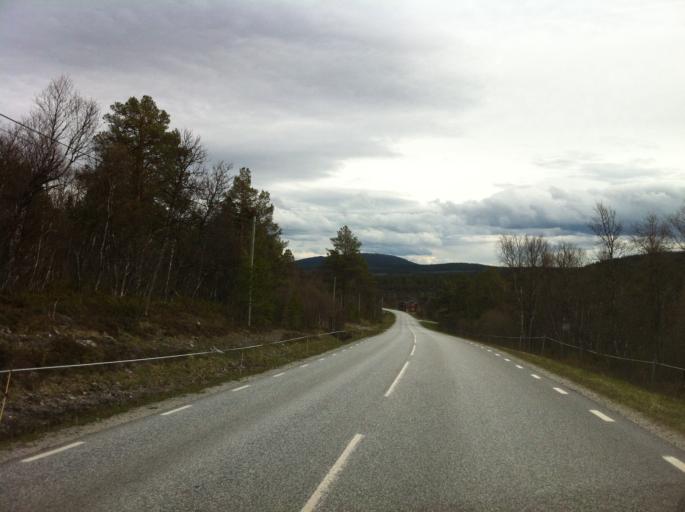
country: NO
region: Sor-Trondelag
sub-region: Tydal
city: Aas
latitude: 62.6341
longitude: 12.4449
